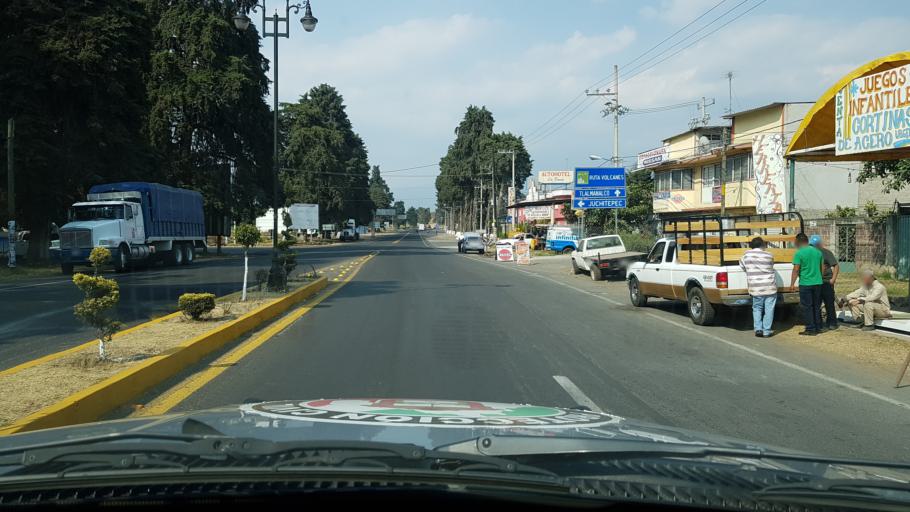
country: MX
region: Mexico
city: Tepetlixpa
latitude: 19.0348
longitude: -98.8098
